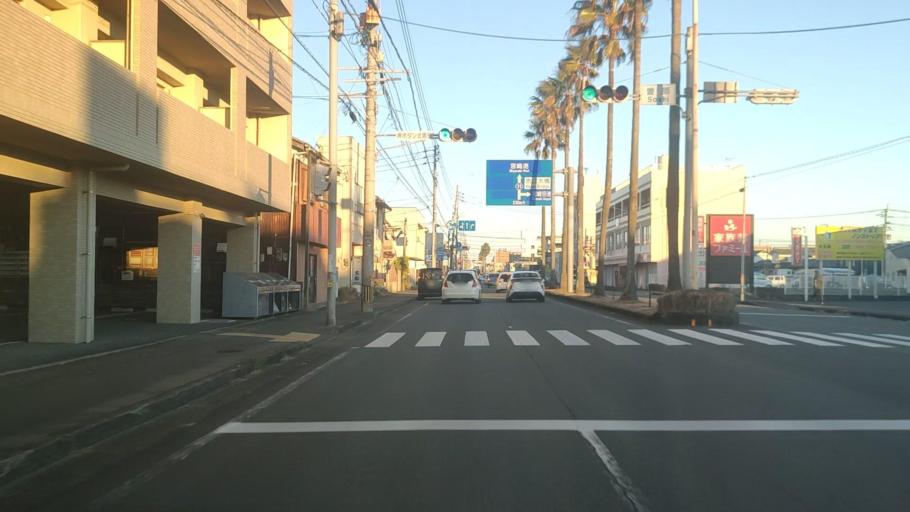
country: JP
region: Miyazaki
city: Miyazaki-shi
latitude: 31.9077
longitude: 131.4396
